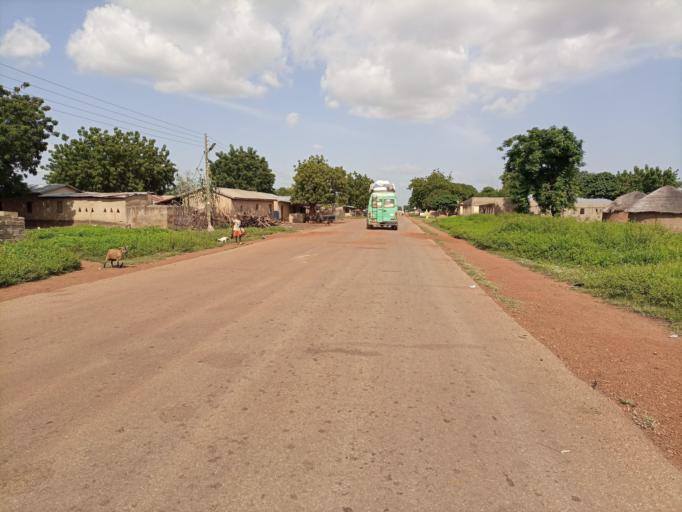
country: GH
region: Northern
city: Savelugu
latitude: 9.5649
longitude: -0.9711
